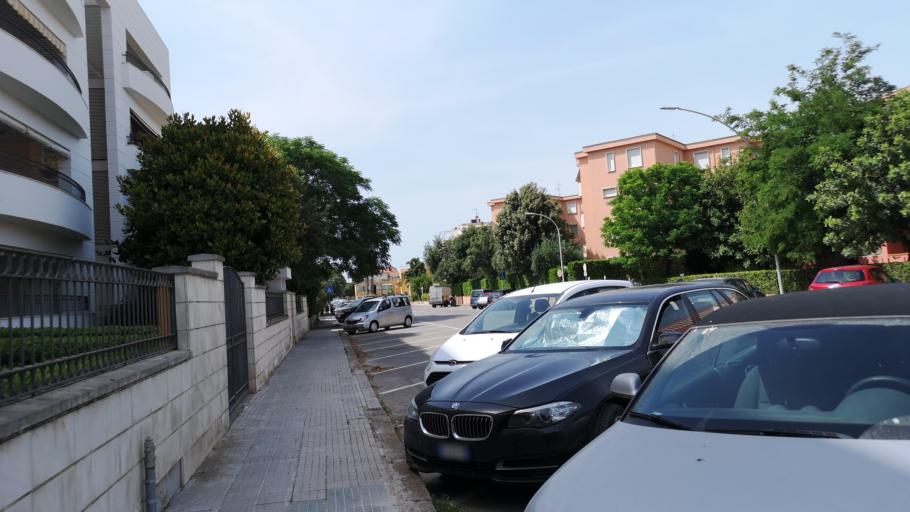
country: IT
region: Sardinia
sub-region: Provincia di Sassari
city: Alghero
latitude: 40.5784
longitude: 8.3150
